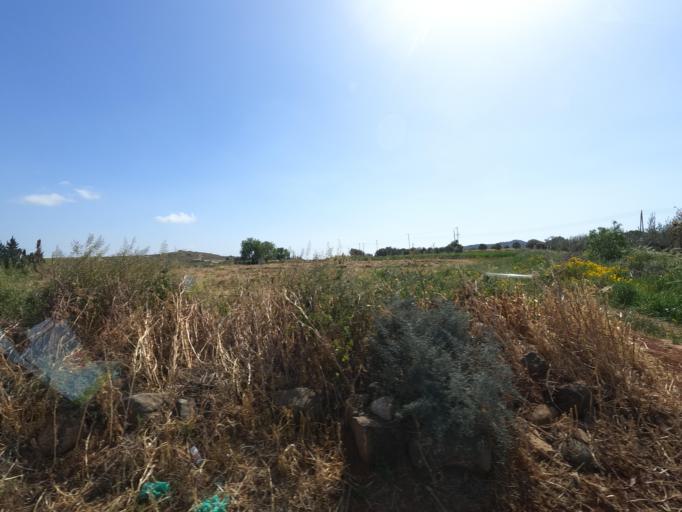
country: CY
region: Lefkosia
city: Astromeritis
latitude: 35.0784
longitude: 33.0160
